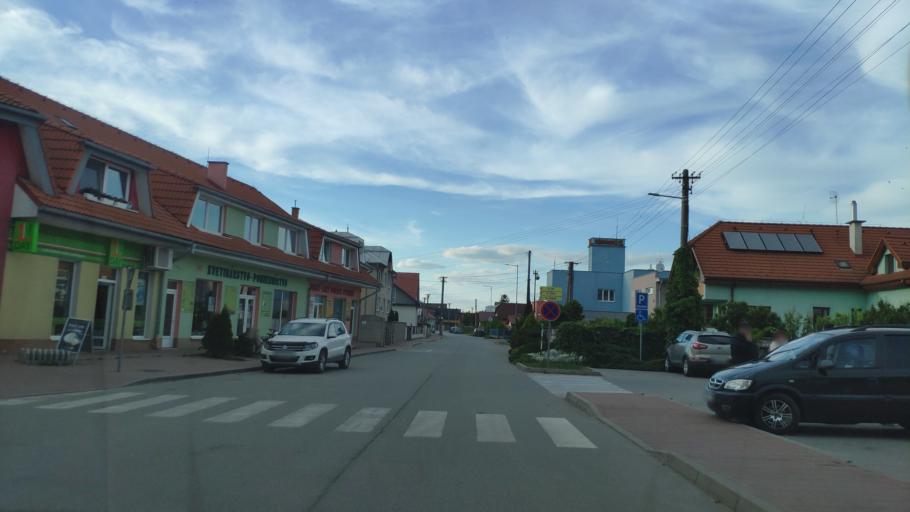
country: SK
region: Kosicky
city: Kosice
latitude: 48.6080
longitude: 21.3259
